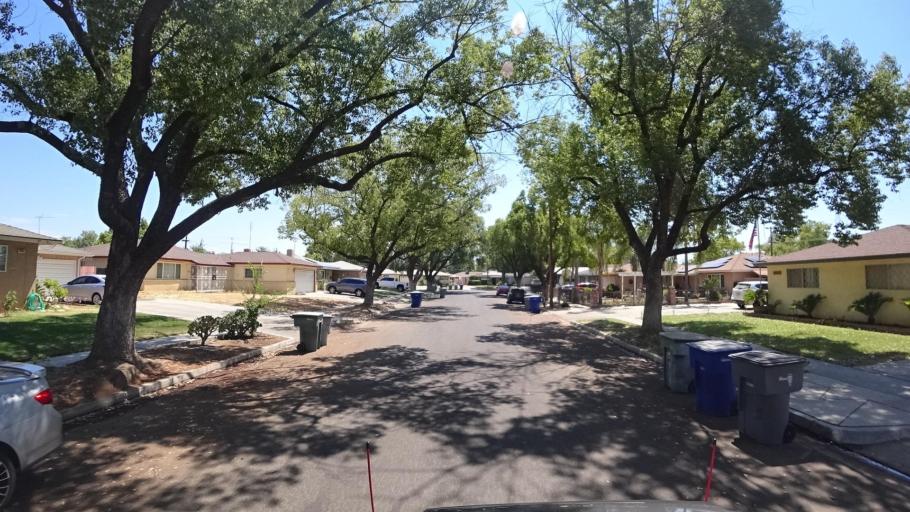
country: US
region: California
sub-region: Fresno County
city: Sunnyside
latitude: 36.7636
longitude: -119.7286
